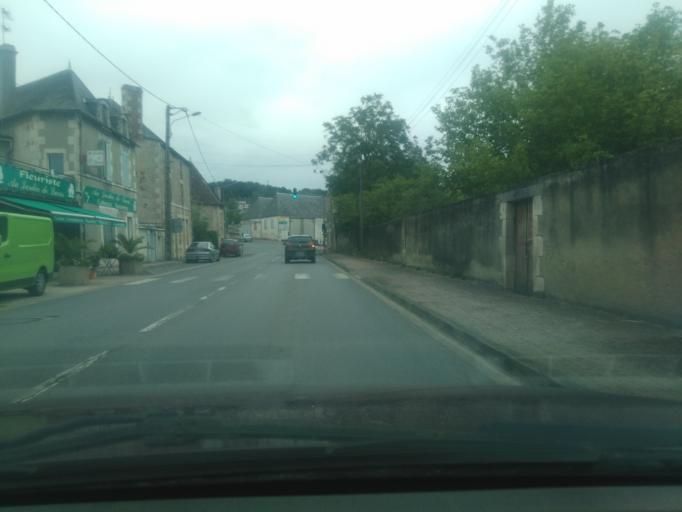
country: FR
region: Poitou-Charentes
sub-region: Departement de la Vienne
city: Saint-Savin
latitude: 46.5637
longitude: 0.8705
